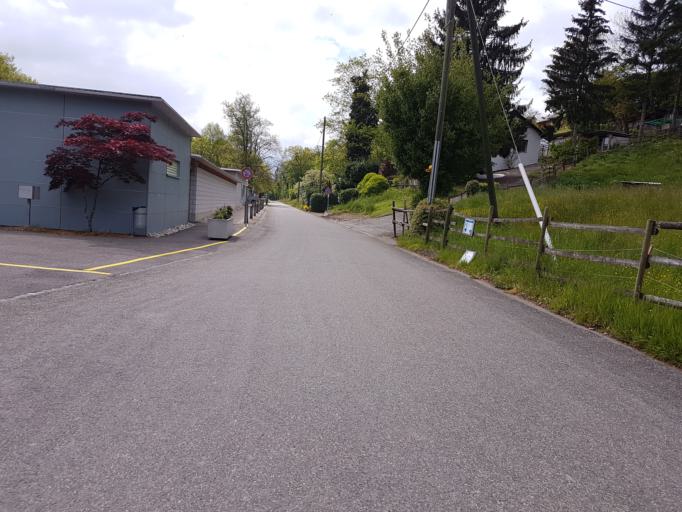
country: CH
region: Aargau
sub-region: Bezirk Brugg
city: Rupperswil
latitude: 47.4130
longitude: 8.1211
